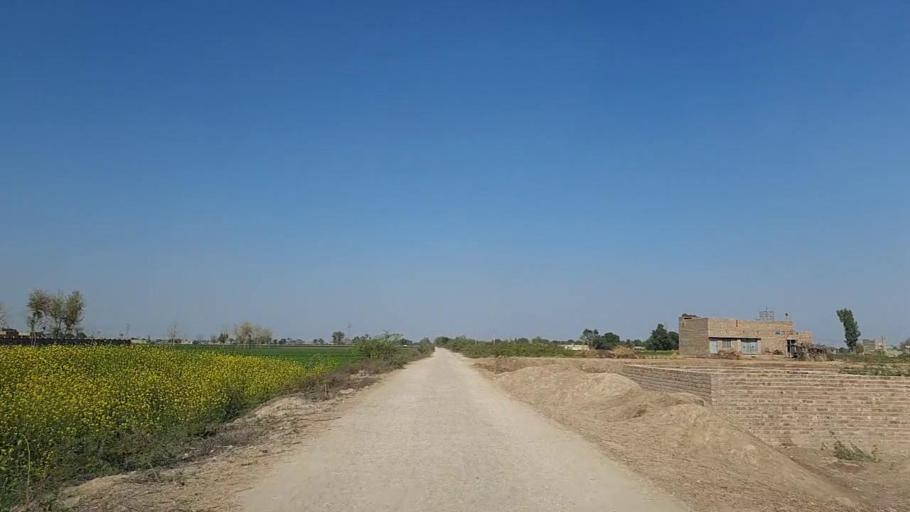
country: PK
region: Sindh
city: Nawabshah
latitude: 26.2460
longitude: 68.4409
